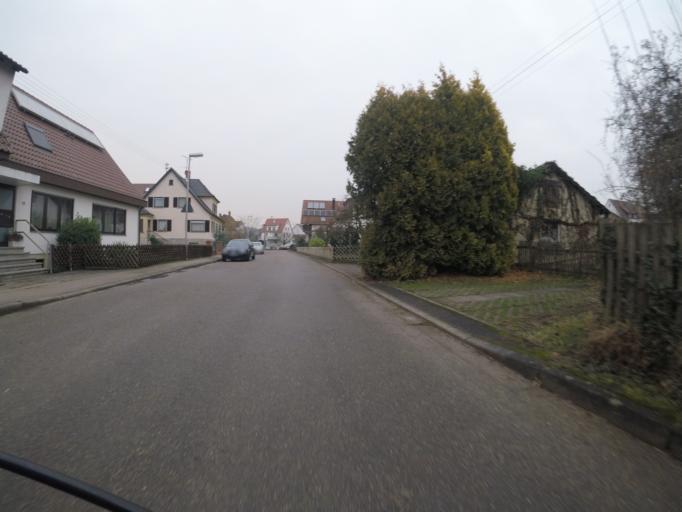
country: DE
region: Baden-Wuerttemberg
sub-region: Regierungsbezirk Stuttgart
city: Kirchberg an der Murr
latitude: 48.9578
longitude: 9.3275
